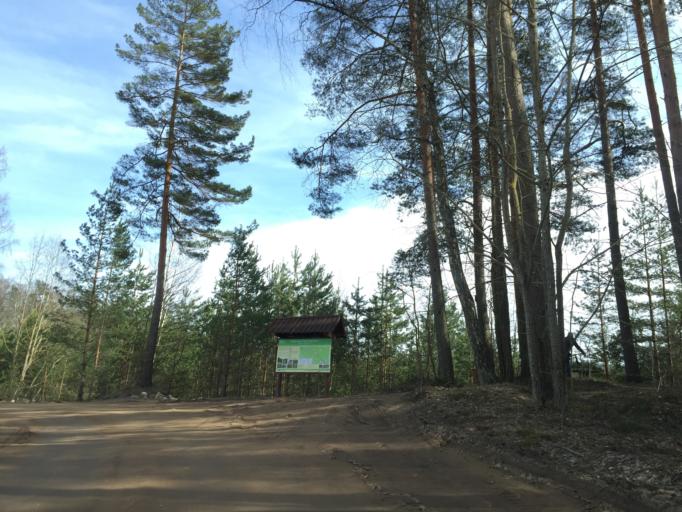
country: LV
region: Ikskile
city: Ikskile
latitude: 56.8431
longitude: 24.5435
